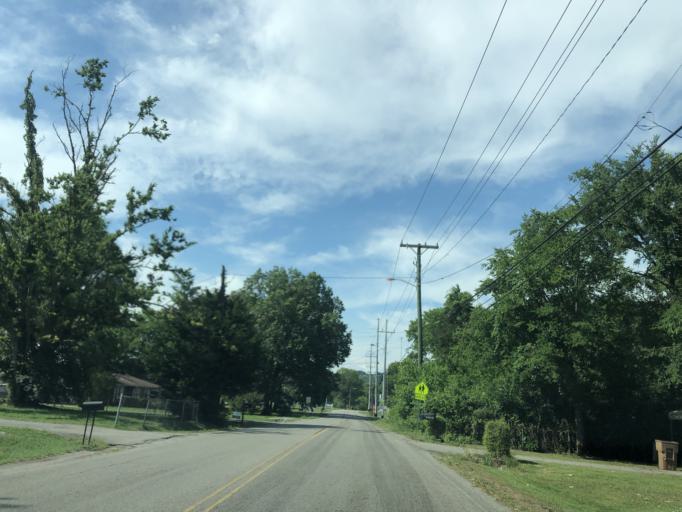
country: US
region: Tennessee
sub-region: Davidson County
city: Nashville
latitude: 36.2355
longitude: -86.8033
